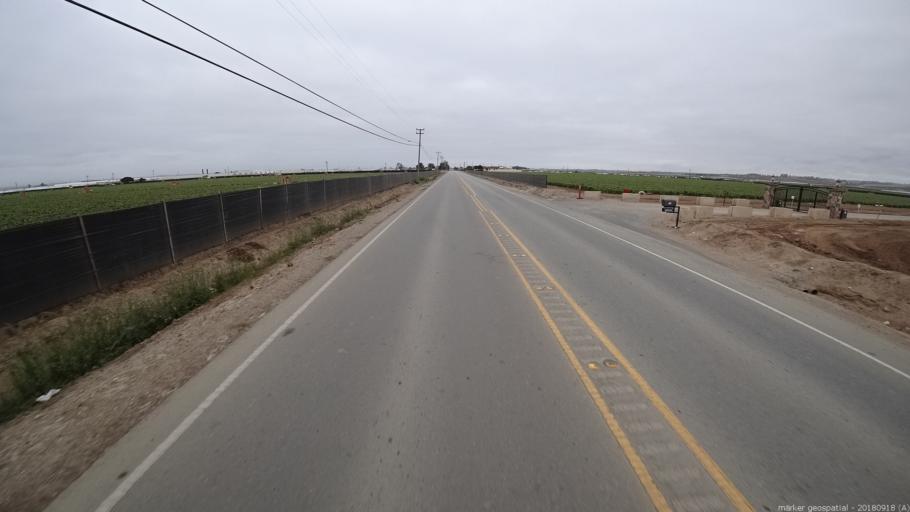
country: US
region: California
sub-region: Monterey County
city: Prunedale
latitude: 36.7380
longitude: -121.6689
